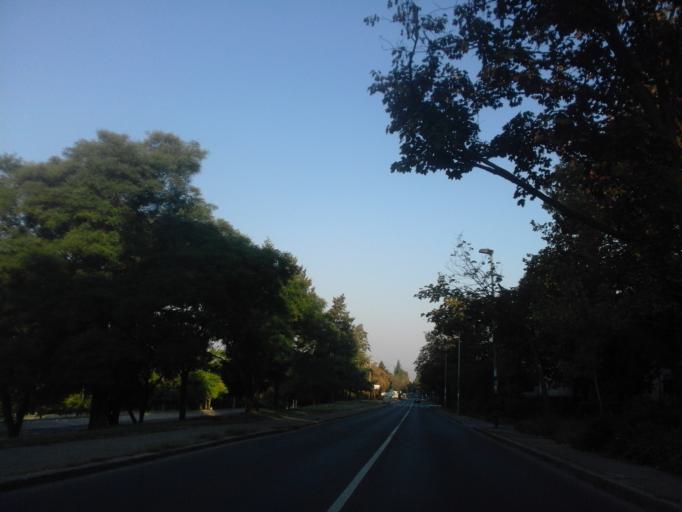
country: RS
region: Central Serbia
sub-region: Belgrade
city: Cukarica
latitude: 44.7653
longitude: 20.4260
